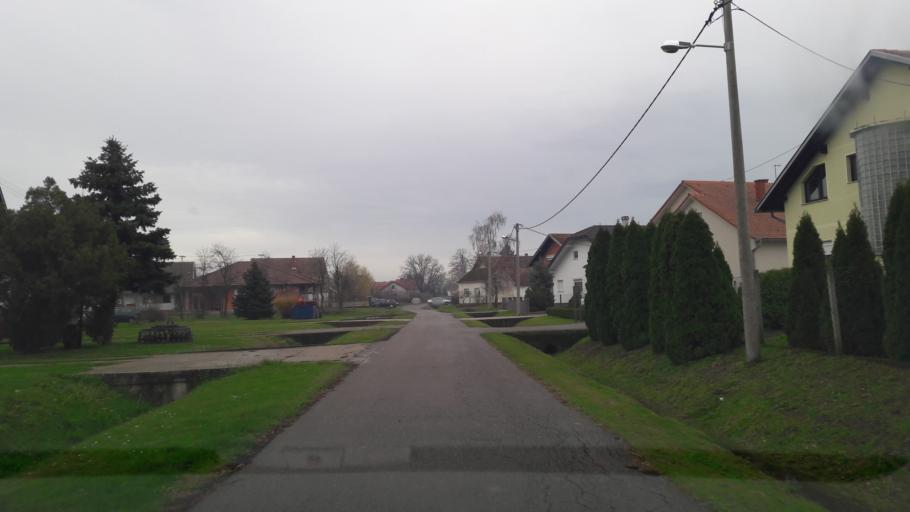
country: HR
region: Osjecko-Baranjska
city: Koska
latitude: 45.5427
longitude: 18.2886
